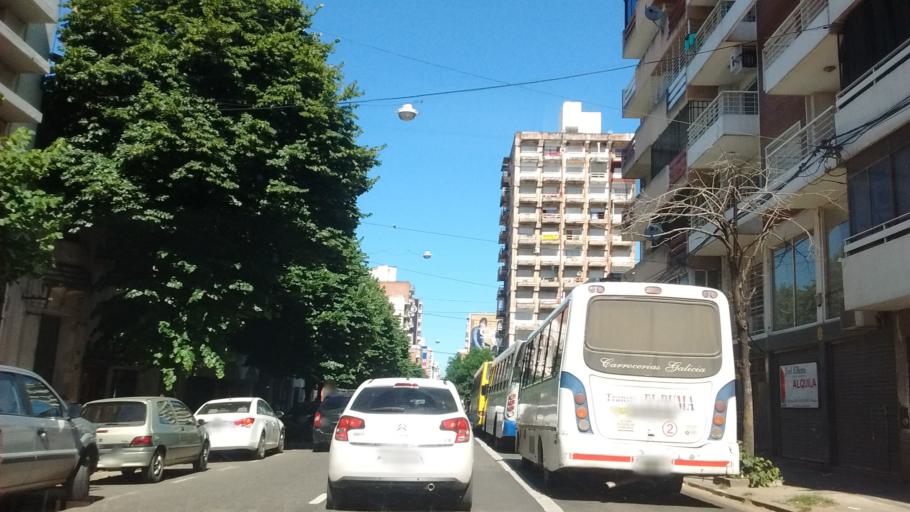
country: AR
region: Santa Fe
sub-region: Departamento de Rosario
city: Rosario
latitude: -32.9414
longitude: -60.6664
